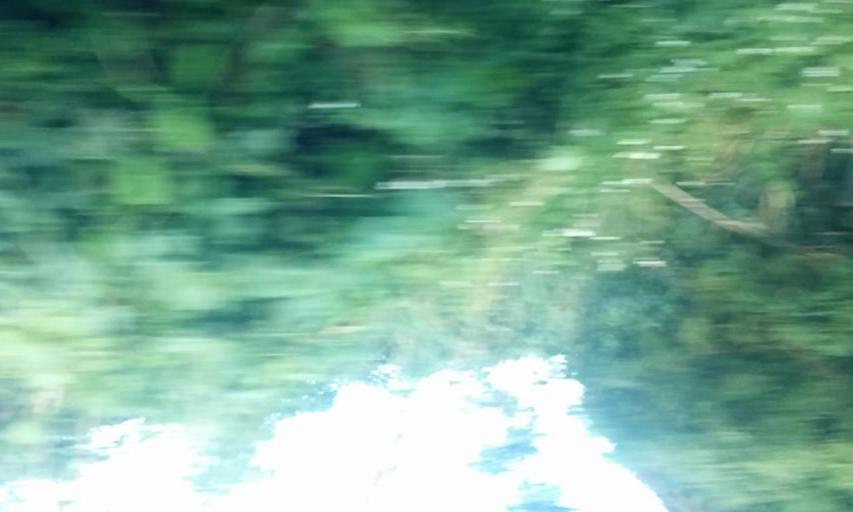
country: JP
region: Kagoshima
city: Nishinoomote
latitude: 30.3584
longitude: 130.6630
